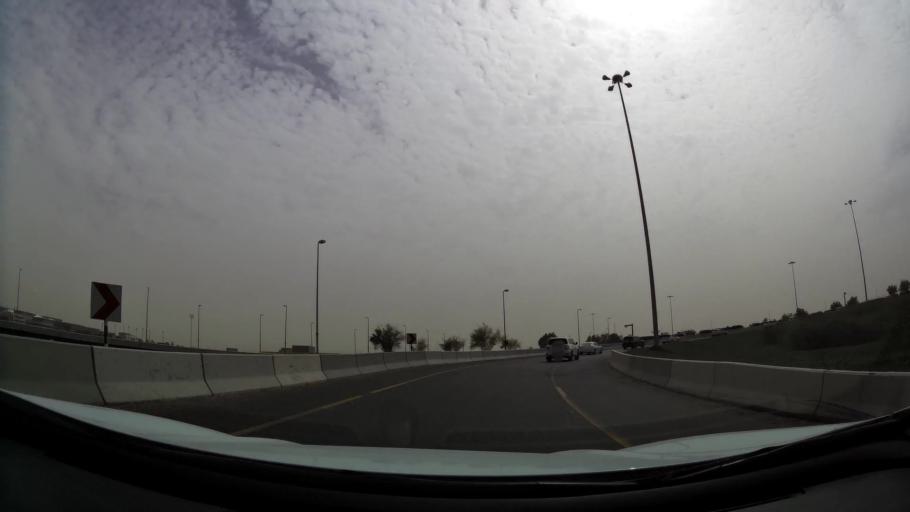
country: AE
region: Abu Dhabi
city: Abu Dhabi
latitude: 24.3966
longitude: 54.5765
